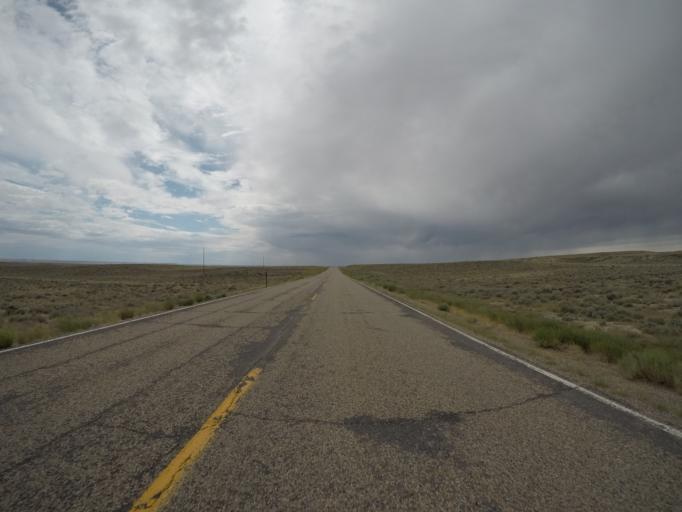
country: US
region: Wyoming
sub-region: Lincoln County
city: Kemmerer
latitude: 41.9670
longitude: -110.0918
